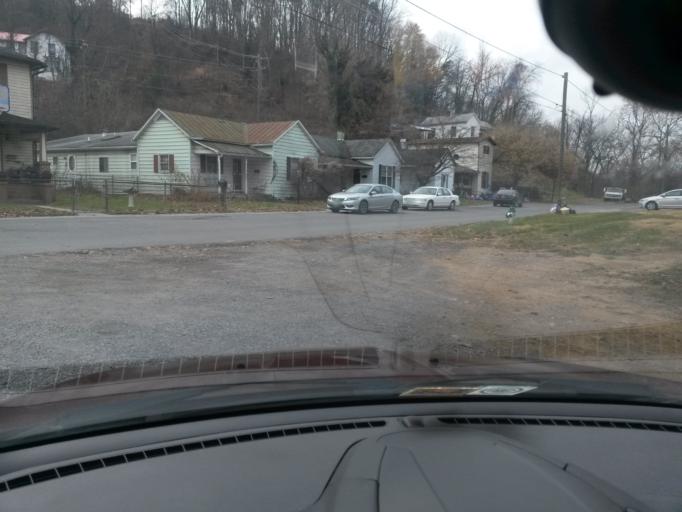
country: US
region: Virginia
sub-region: Alleghany County
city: Clifton Forge
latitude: 37.8135
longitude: -79.8250
